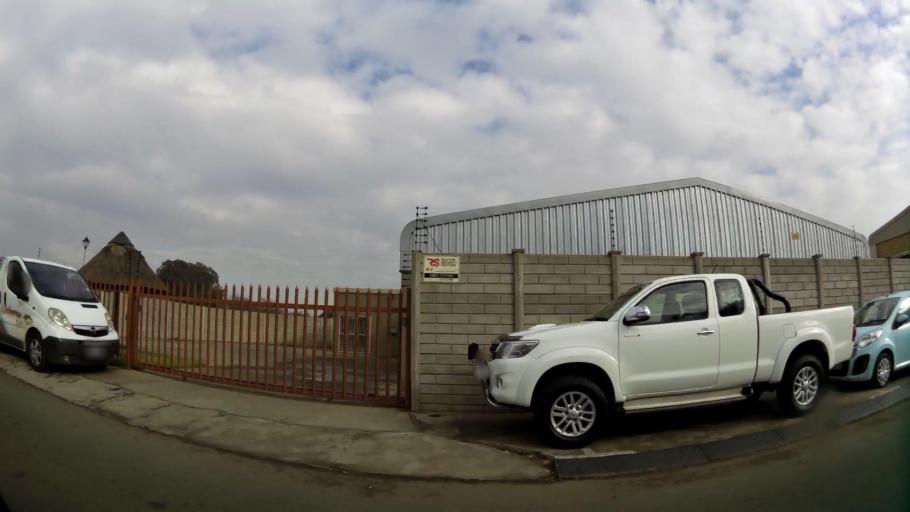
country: ZA
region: Gauteng
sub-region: Sedibeng District Municipality
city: Vanderbijlpark
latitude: -26.6952
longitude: 27.8321
